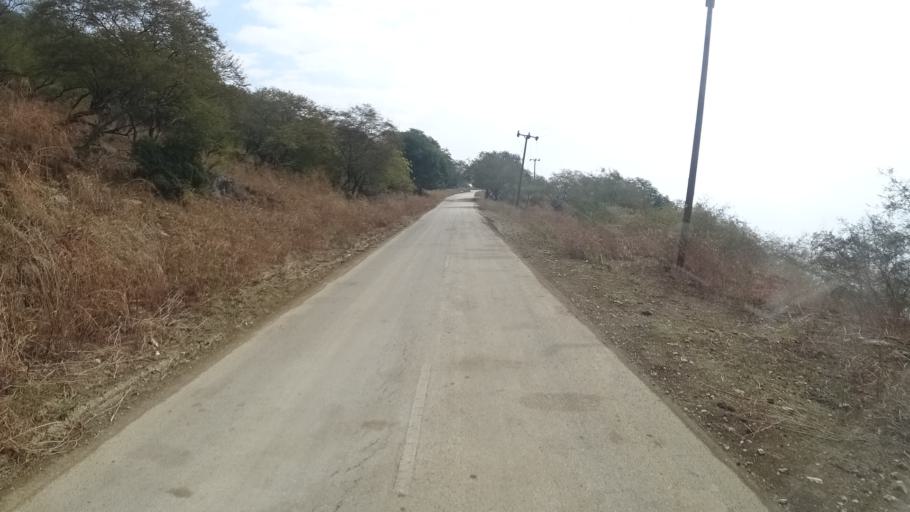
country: YE
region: Al Mahrah
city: Hawf
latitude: 16.7111
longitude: 53.2325
